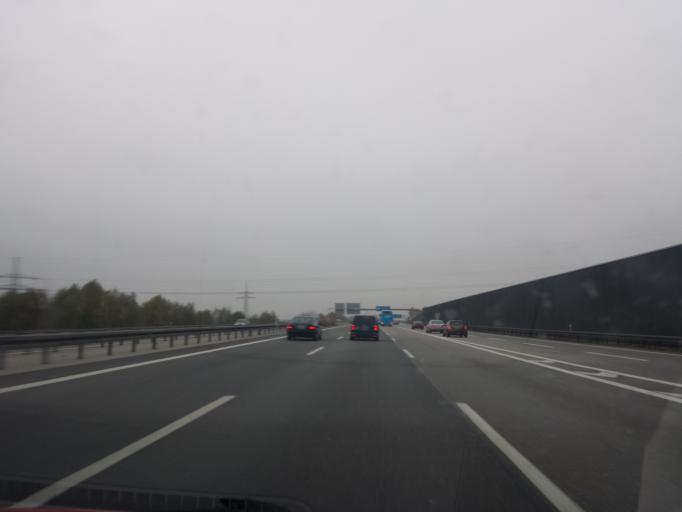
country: DE
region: Bavaria
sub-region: Upper Bavaria
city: Eching
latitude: 48.3110
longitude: 11.6240
